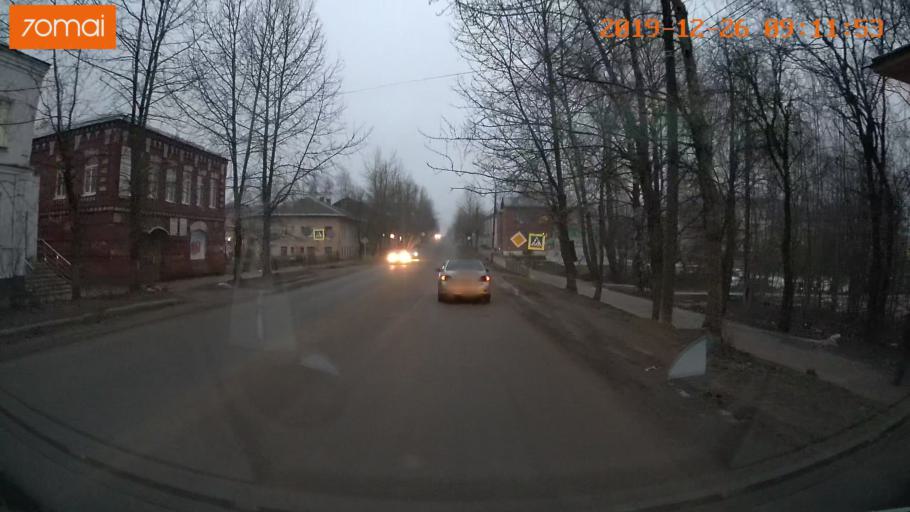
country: RU
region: Vologda
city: Gryazovets
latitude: 58.8781
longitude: 40.2530
